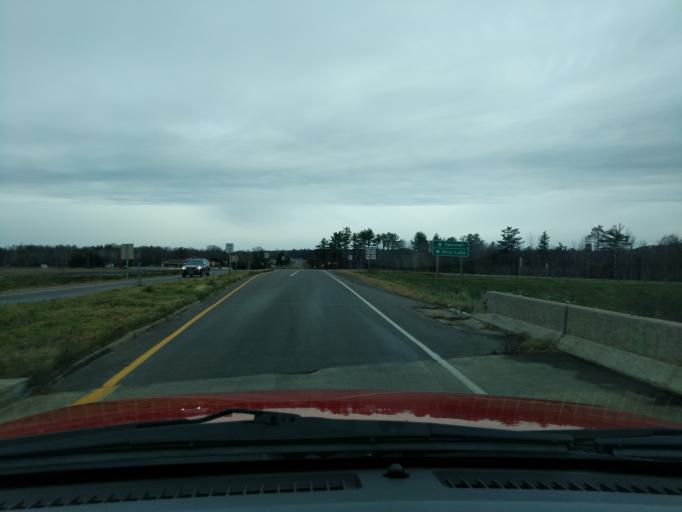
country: US
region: Wisconsin
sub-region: Washburn County
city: Spooner
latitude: 45.8178
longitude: -91.8566
